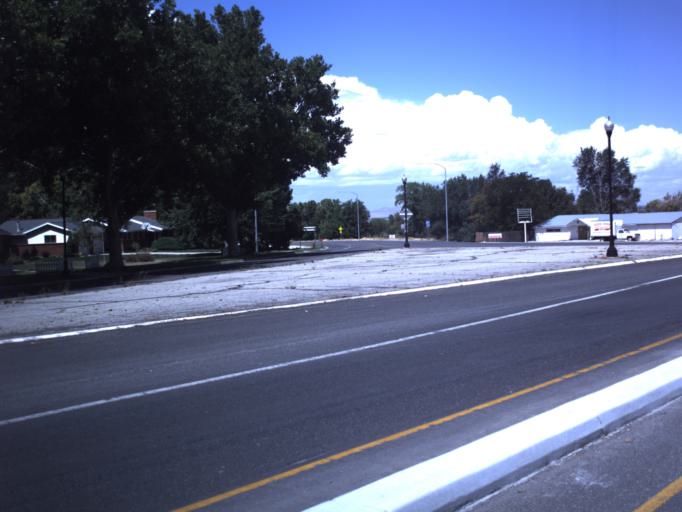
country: US
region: Utah
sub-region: Box Elder County
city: Brigham City
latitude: 41.5276
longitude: -112.0155
